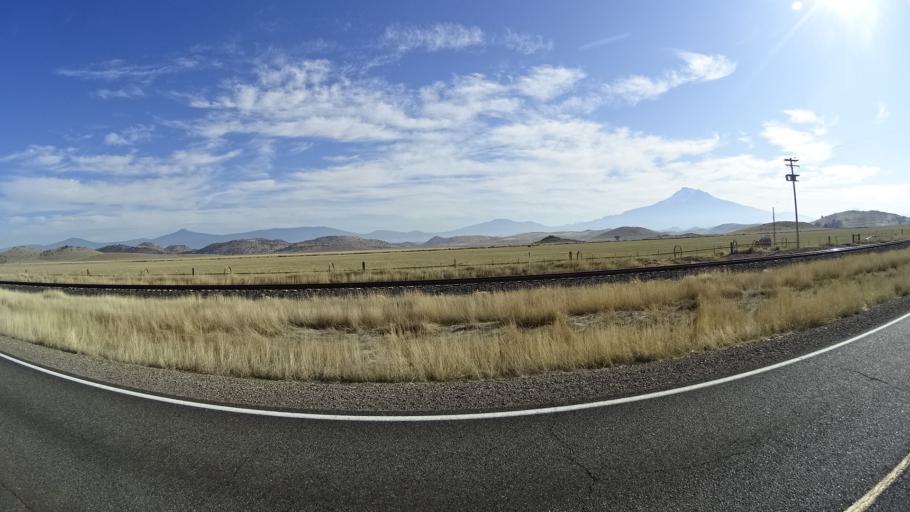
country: US
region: California
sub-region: Siskiyou County
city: Montague
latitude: 41.5714
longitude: -122.5252
